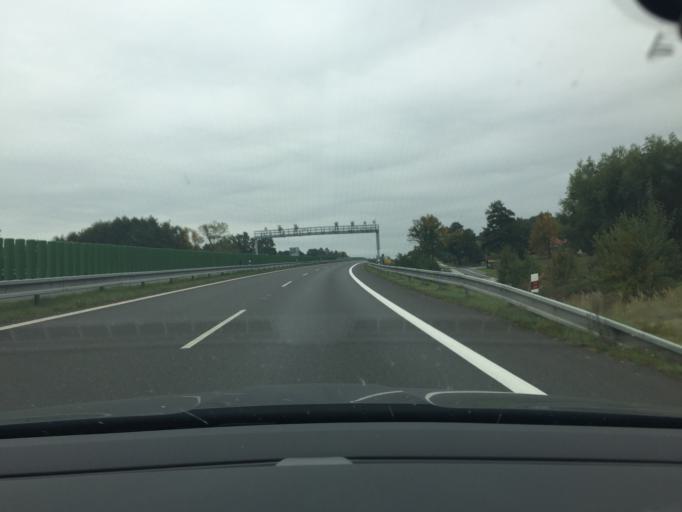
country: CZ
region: Jihocesky
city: Mirotice
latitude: 49.3910
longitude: 14.0479
